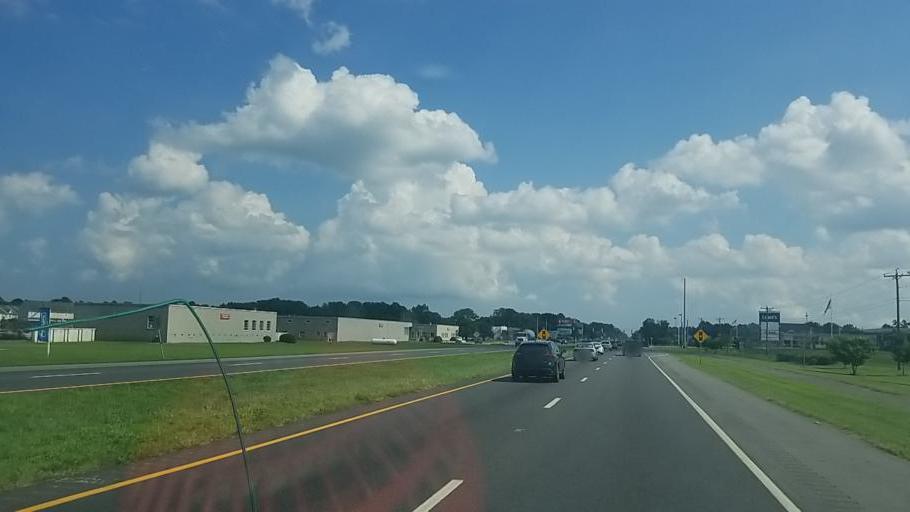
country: US
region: Delaware
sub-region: Sussex County
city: Millsboro
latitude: 38.5739
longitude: -75.2852
